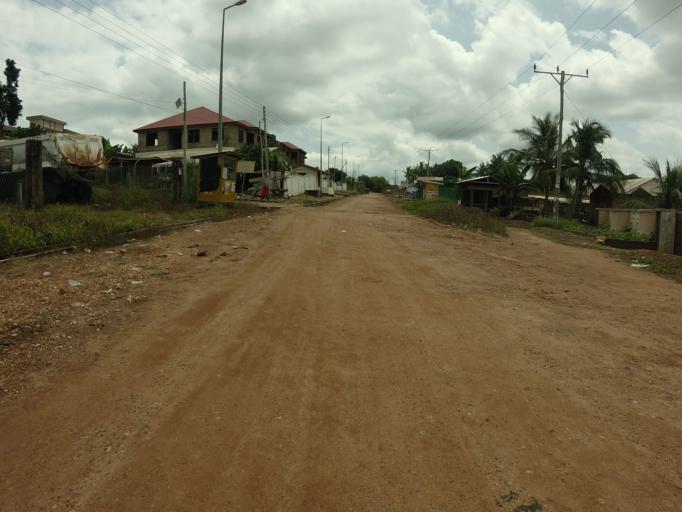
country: GH
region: Volta
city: Ho
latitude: 6.5951
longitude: 0.4693
